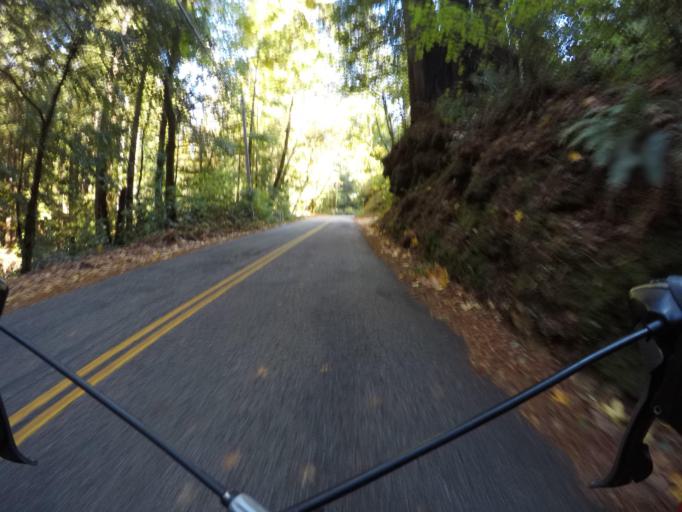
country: US
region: California
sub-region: Santa Cruz County
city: Scotts Valley
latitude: 37.0968
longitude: -121.9983
